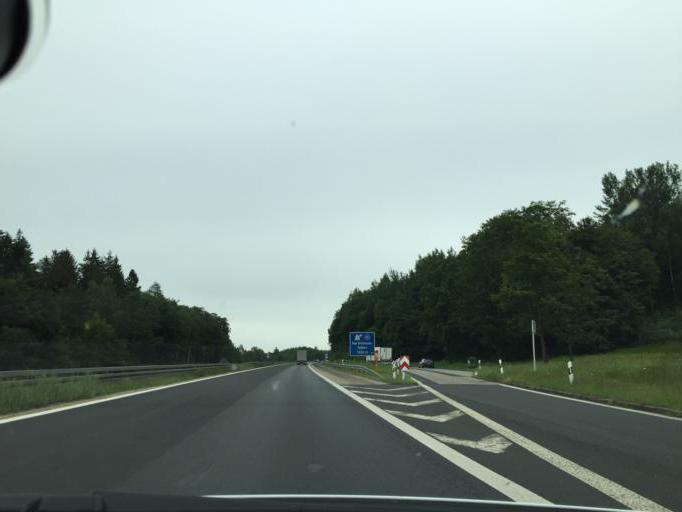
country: DE
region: Bavaria
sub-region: Regierungsbezirk Unterfranken
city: Bad Bruckenau
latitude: 50.3454
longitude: 9.7565
